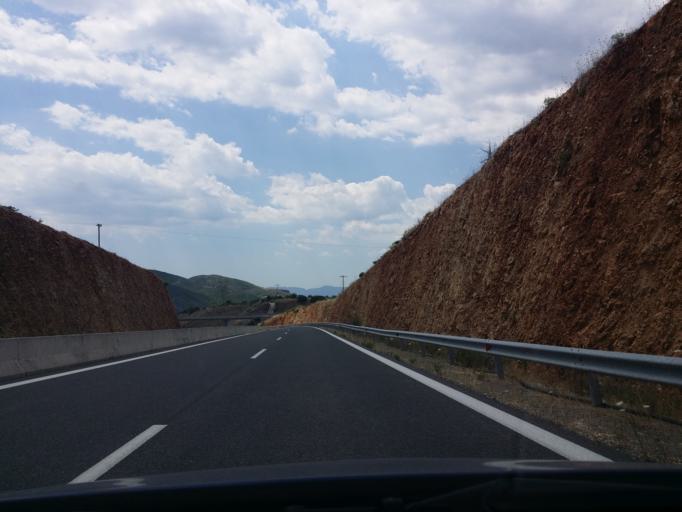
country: GR
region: Peloponnese
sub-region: Nomos Arkadias
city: Megalopoli
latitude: 37.3089
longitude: 22.1801
